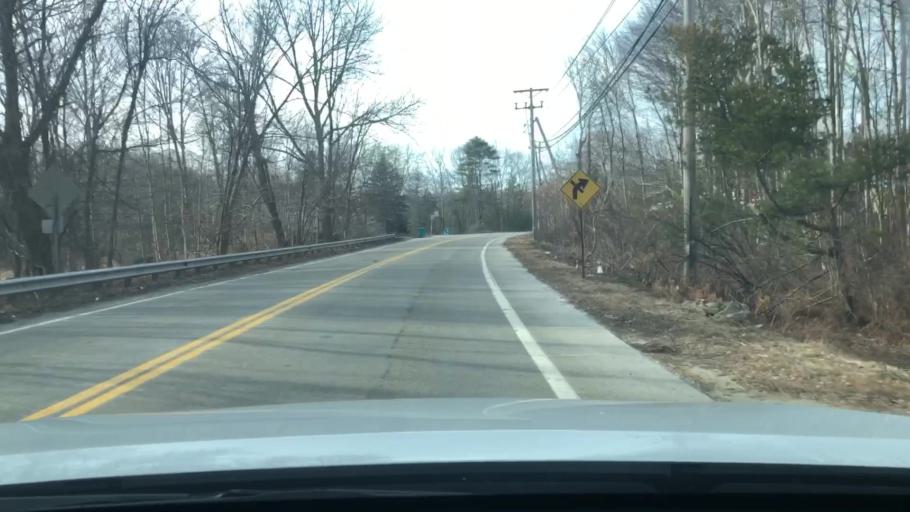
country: US
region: Massachusetts
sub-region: Worcester County
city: Upton
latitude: 42.1549
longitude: -71.5741
